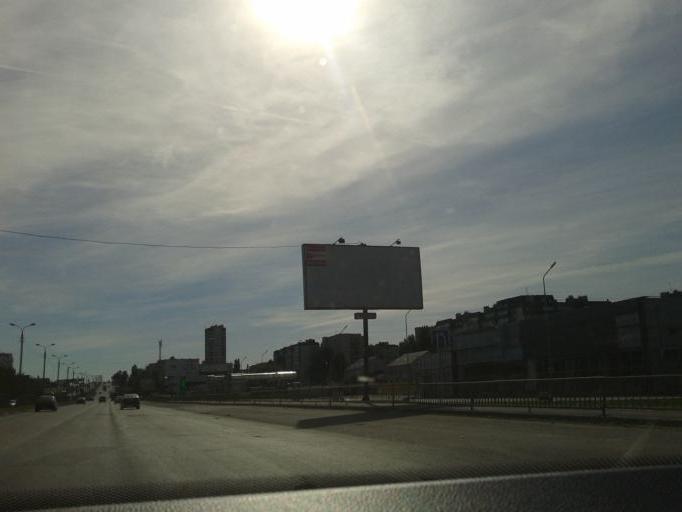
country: RU
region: Volgograd
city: Volgograd
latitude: 48.7586
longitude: 44.4973
